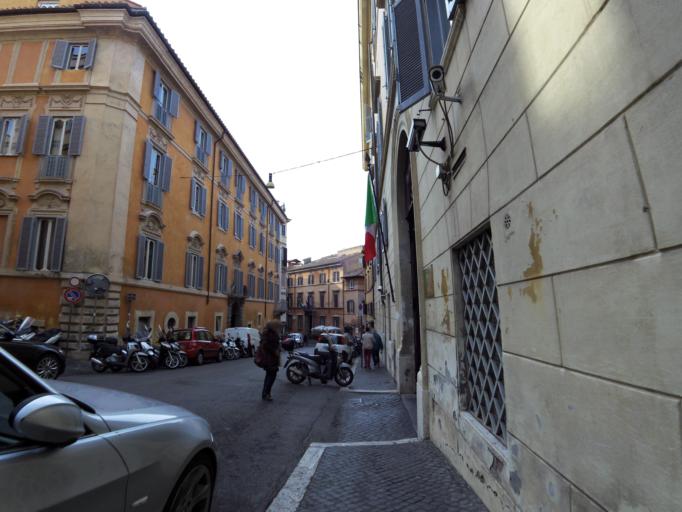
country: IT
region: Latium
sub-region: Citta metropolitana di Roma Capitale
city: Rome
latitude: 41.9000
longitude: 12.4845
